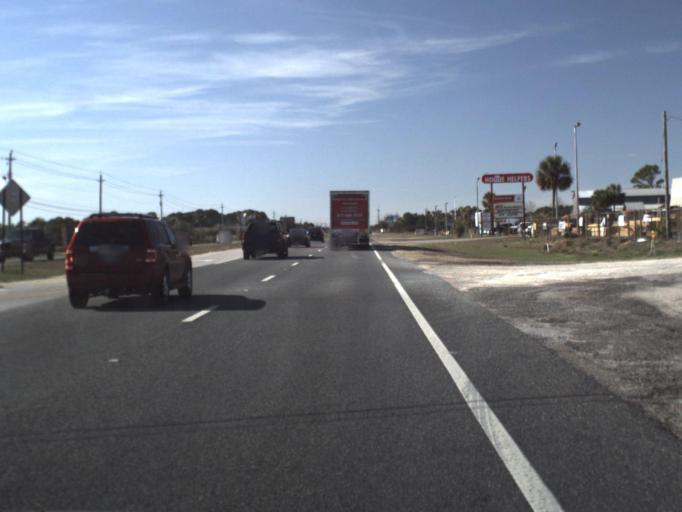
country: US
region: Florida
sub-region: Bay County
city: Laguna Beach
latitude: 30.2379
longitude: -85.9074
